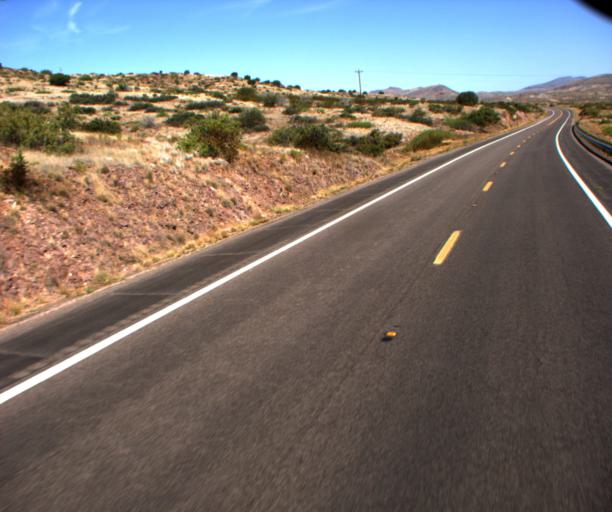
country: US
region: Arizona
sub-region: Greenlee County
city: Clifton
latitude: 32.7559
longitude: -109.2417
